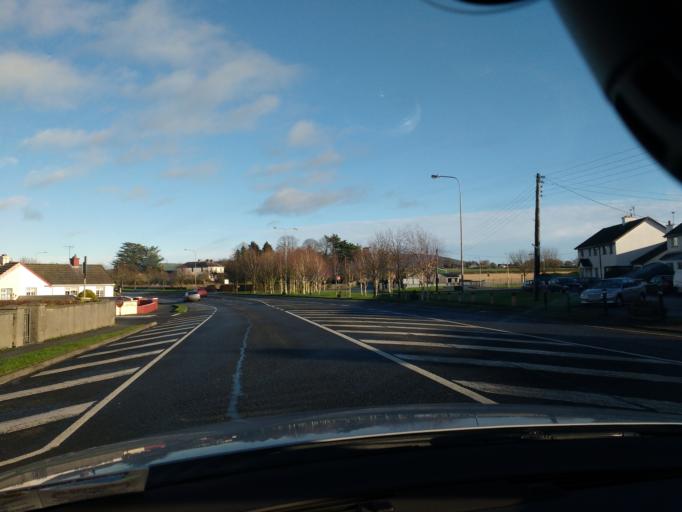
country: IE
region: Leinster
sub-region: Laois
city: Rathdowney
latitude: 52.7227
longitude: -7.5777
